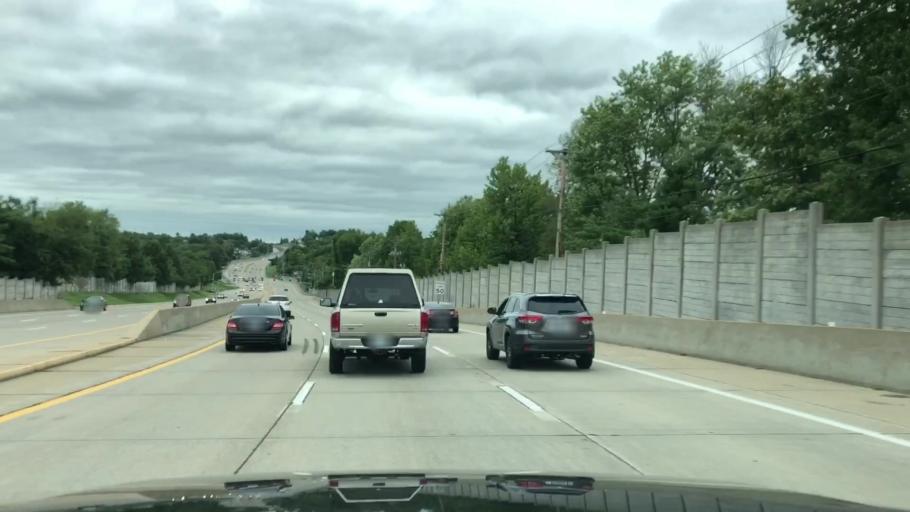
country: US
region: Missouri
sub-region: Saint Louis County
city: Manchester
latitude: 38.6147
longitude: -90.5124
